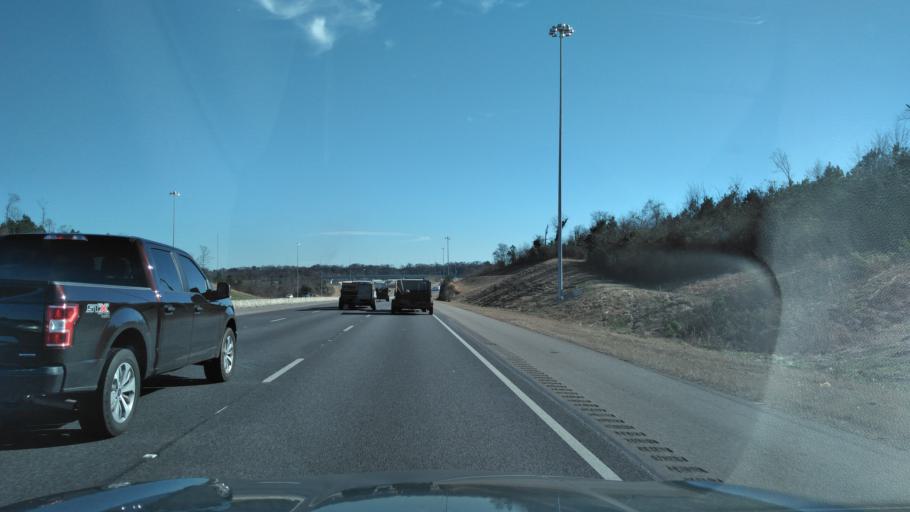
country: US
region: Alabama
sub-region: Jefferson County
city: Fultondale
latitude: 33.5816
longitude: -86.8271
